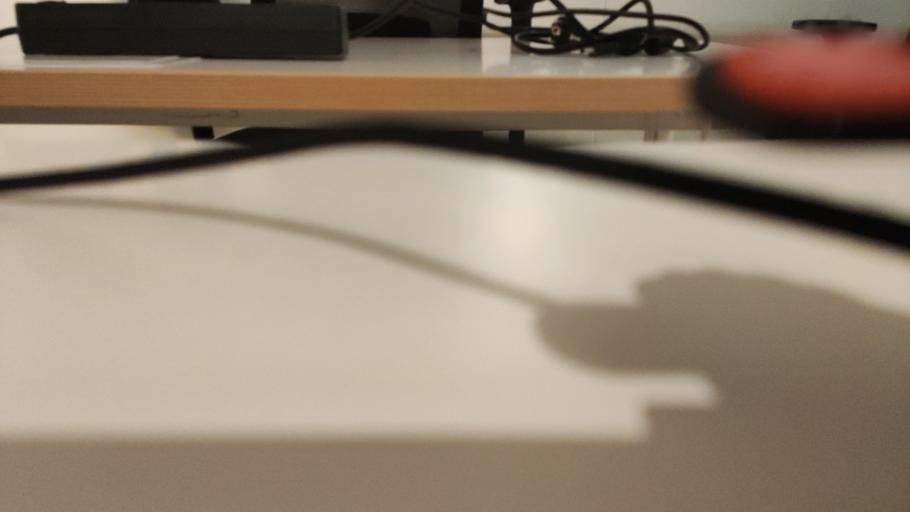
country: RU
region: Moskovskaya
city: Proletarskiy
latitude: 54.9757
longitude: 37.4024
